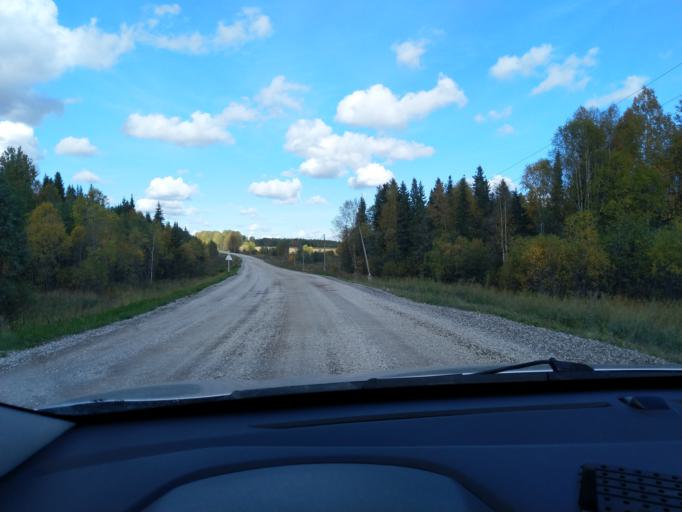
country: RU
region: Perm
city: Usol'ye
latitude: 59.4648
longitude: 56.3700
